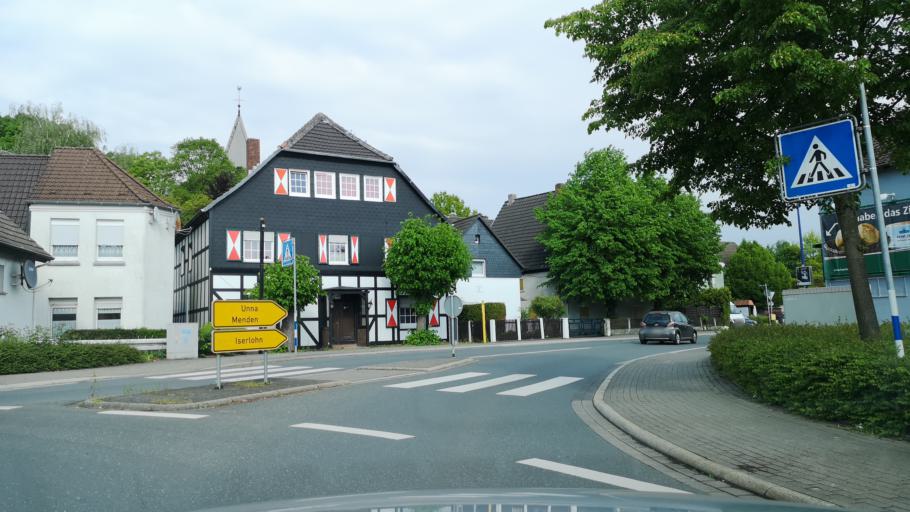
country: DE
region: North Rhine-Westphalia
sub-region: Regierungsbezirk Arnsberg
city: Holzwickede
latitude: 51.4452
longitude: 7.6482
